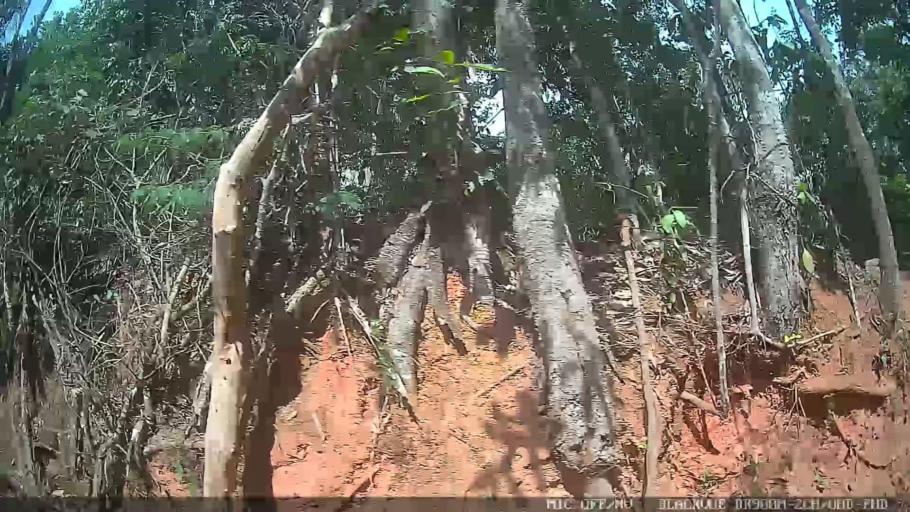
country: BR
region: Sao Paulo
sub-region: Atibaia
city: Atibaia
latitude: -23.0805
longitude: -46.5421
